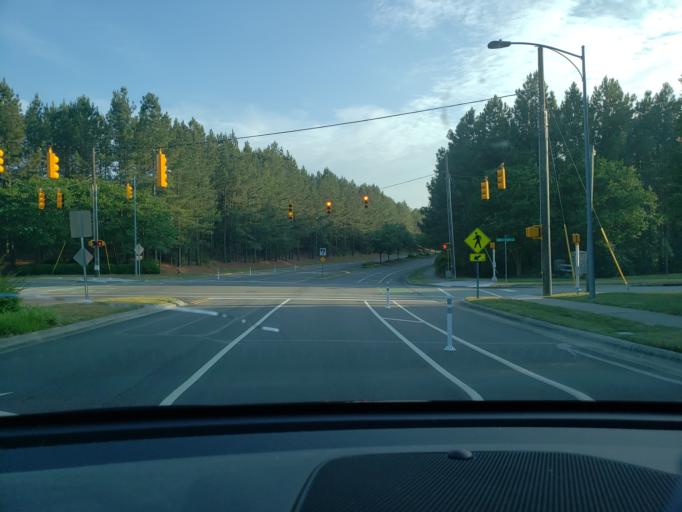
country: US
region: North Carolina
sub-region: Durham County
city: Durham
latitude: 35.9390
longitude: -78.9291
